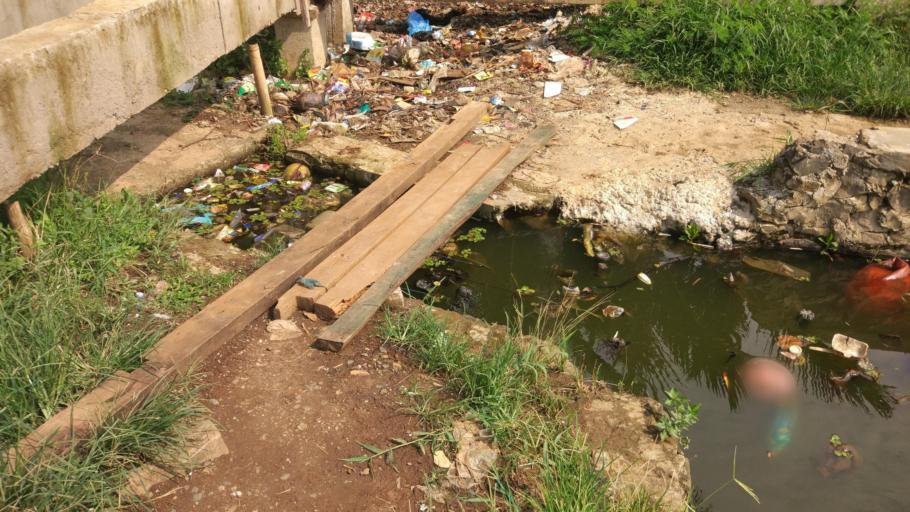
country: ID
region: West Java
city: Ciampea
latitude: -6.5547
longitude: 106.7502
